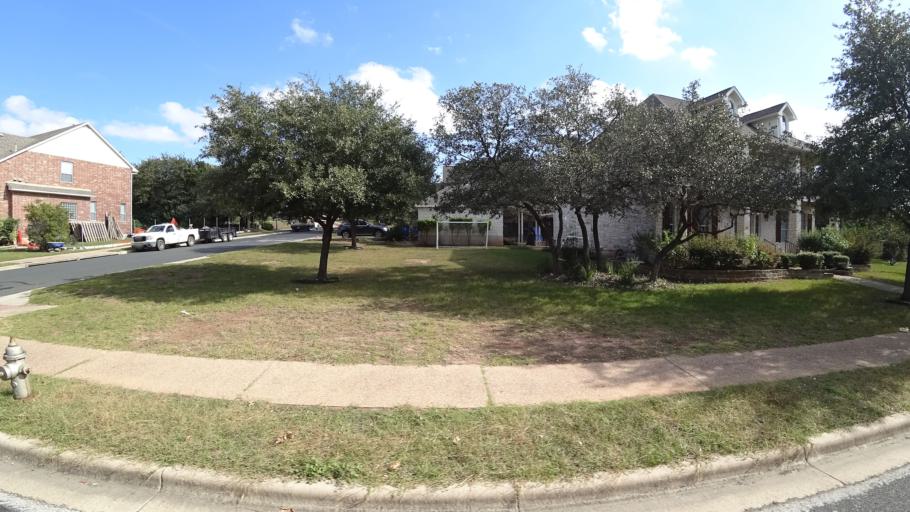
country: US
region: Texas
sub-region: Williamson County
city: Anderson Mill
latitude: 30.4277
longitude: -97.8125
